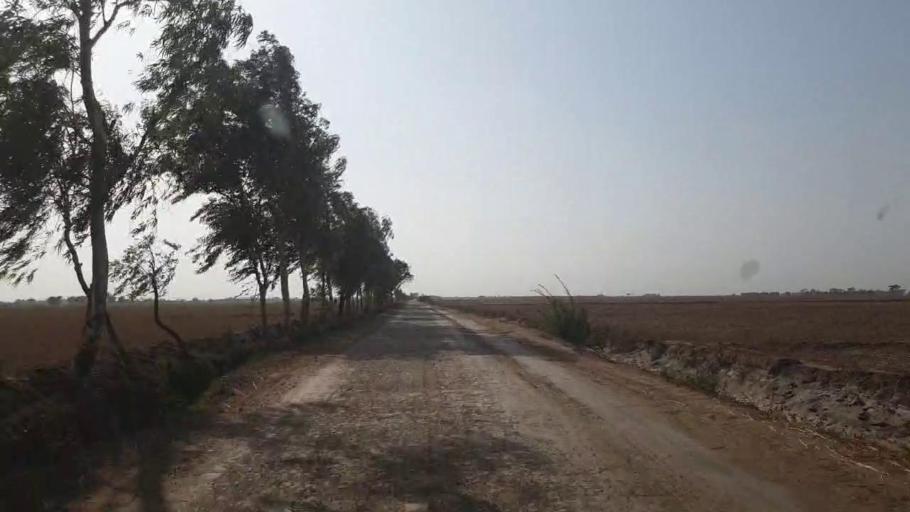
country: PK
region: Sindh
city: Kario
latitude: 24.5765
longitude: 68.5160
